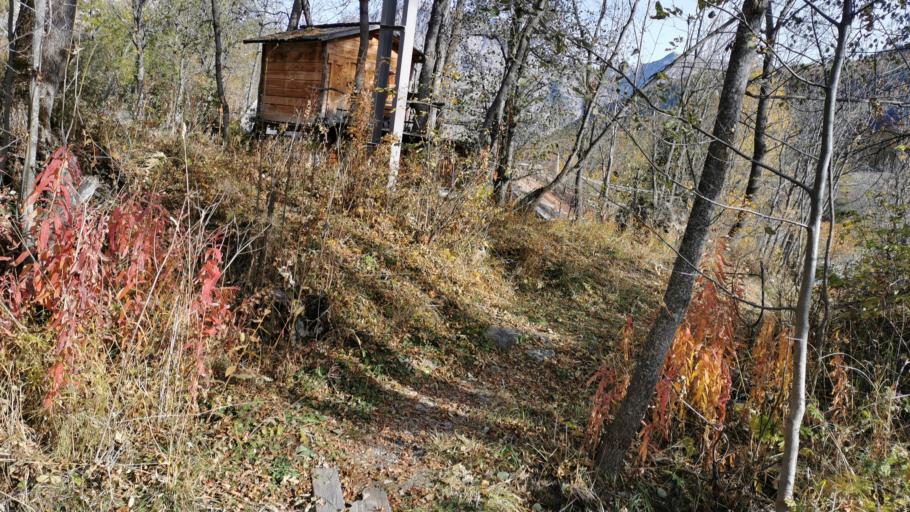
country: FR
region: Provence-Alpes-Cote d'Azur
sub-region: Departement des Hautes-Alpes
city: Villeneuve
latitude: 45.0193
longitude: 6.6009
